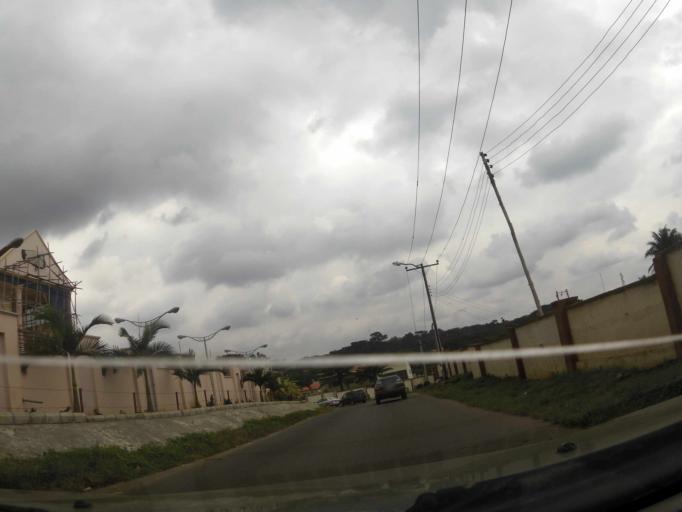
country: NG
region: Oyo
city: Ibadan
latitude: 7.4042
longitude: 3.9241
